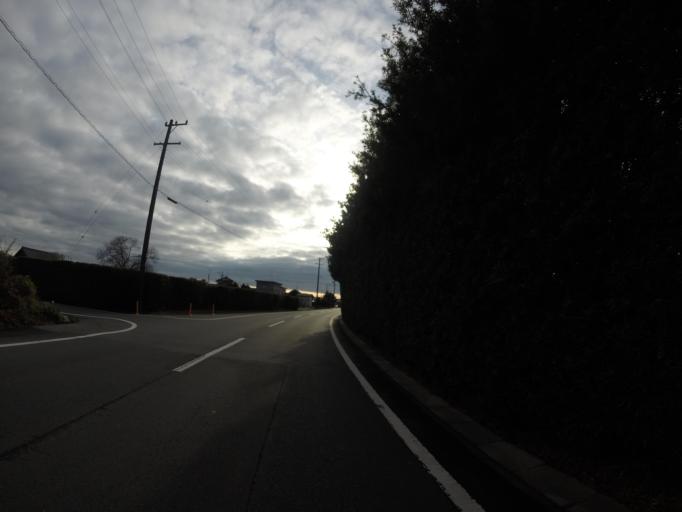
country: JP
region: Shizuoka
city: Hamakita
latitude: 34.8187
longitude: 137.7706
